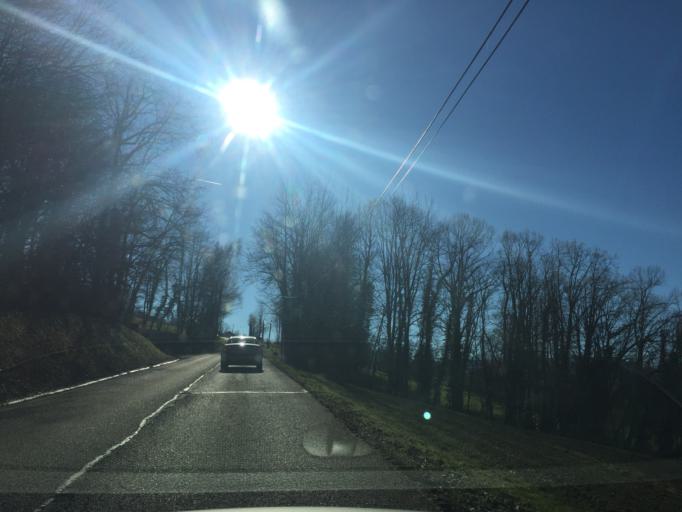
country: FR
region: Rhone-Alpes
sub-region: Departement de la Savoie
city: Gresy-sur-Aix
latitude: 45.7055
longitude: 5.9710
